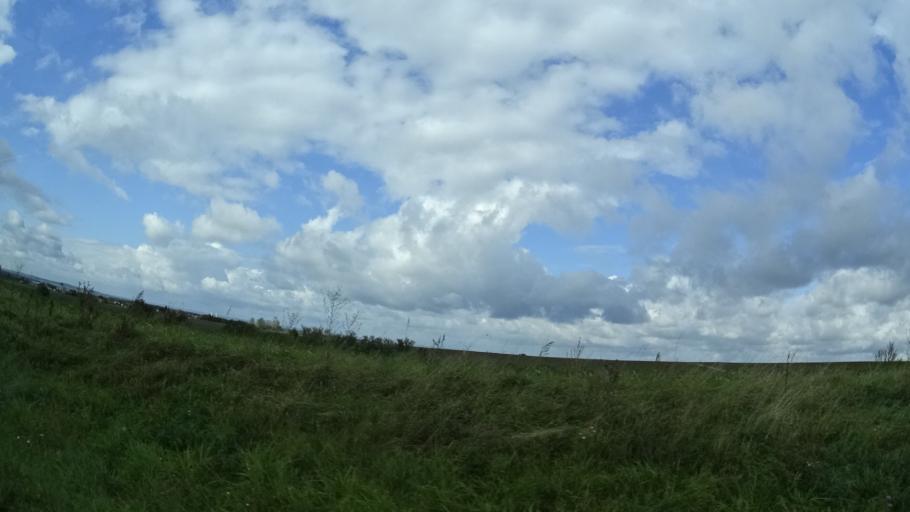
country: DE
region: Bavaria
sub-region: Regierungsbezirk Unterfranken
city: Dingolshausen
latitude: 49.9036
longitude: 10.3773
